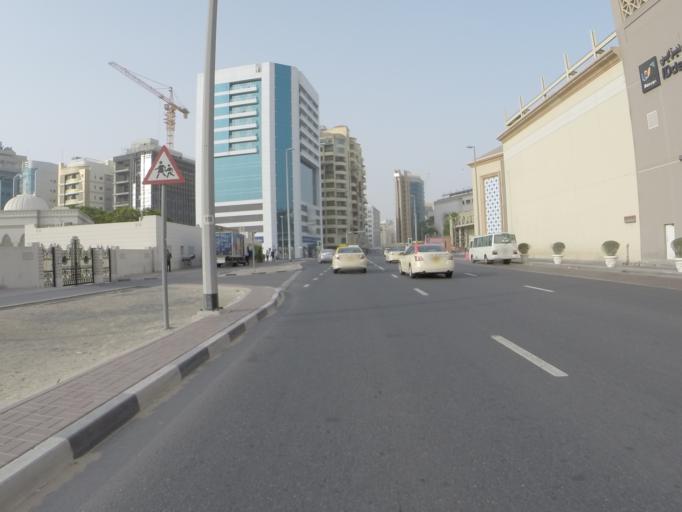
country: AE
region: Dubai
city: Dubai
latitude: 25.1190
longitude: 55.2043
